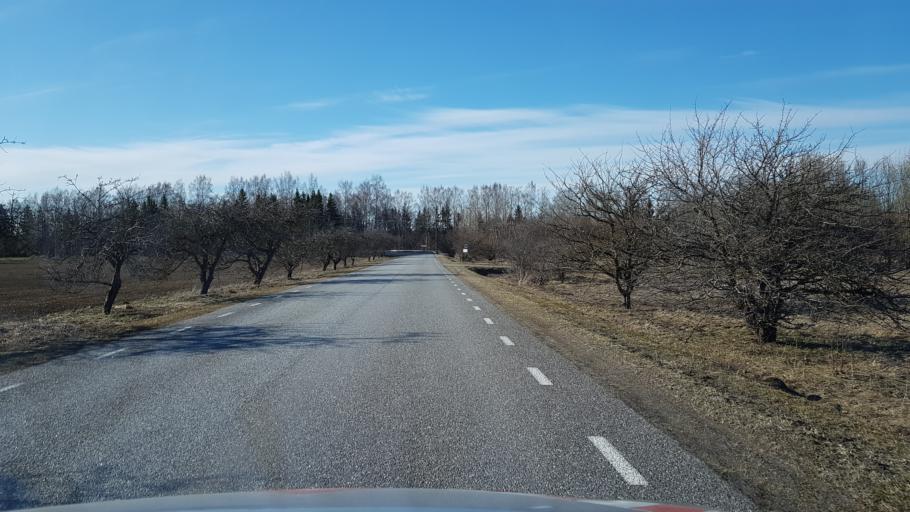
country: EE
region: Laeaene-Virumaa
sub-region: Kadrina vald
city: Kadrina
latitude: 59.3353
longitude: 26.1273
